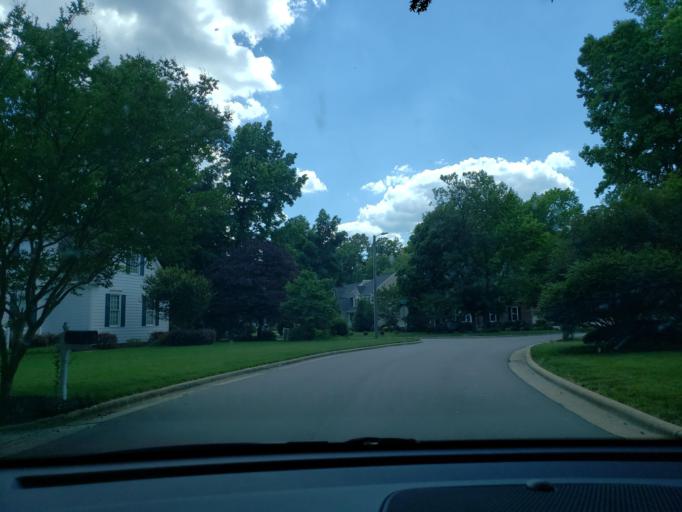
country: US
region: North Carolina
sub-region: Orange County
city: Chapel Hill
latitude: 35.9670
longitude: -78.9907
